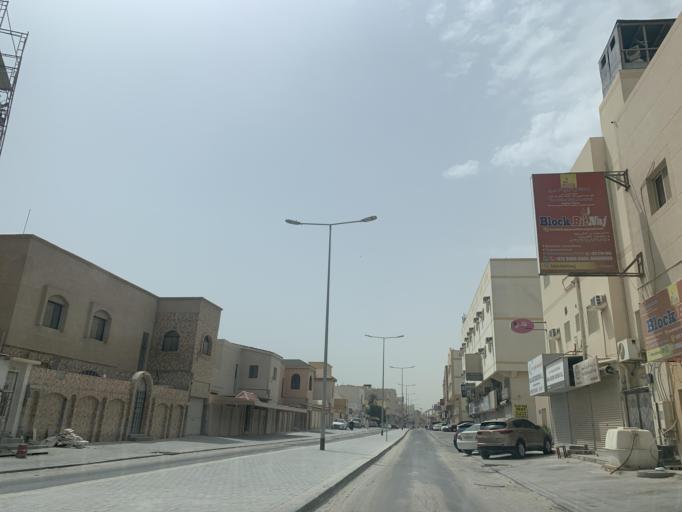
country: BH
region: Northern
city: Ar Rifa'
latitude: 26.1288
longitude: 50.5633
